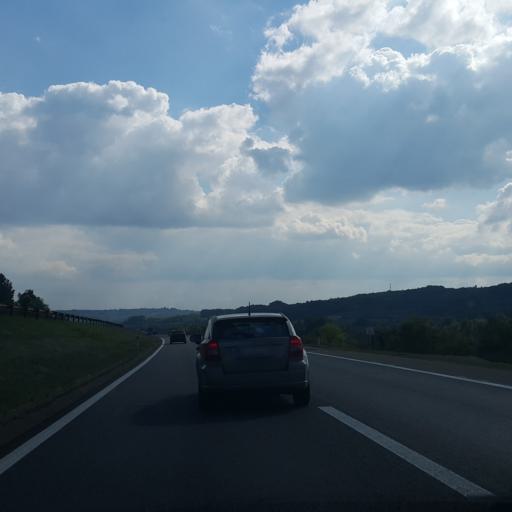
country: RS
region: Central Serbia
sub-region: Belgrade
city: Sopot
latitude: 44.5929
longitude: 20.6395
